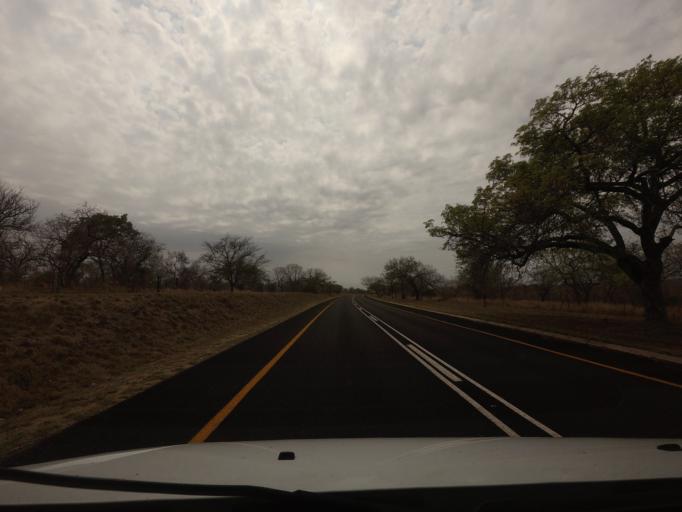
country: ZA
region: Limpopo
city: Thulamahashi
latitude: -24.5539
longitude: 31.1850
